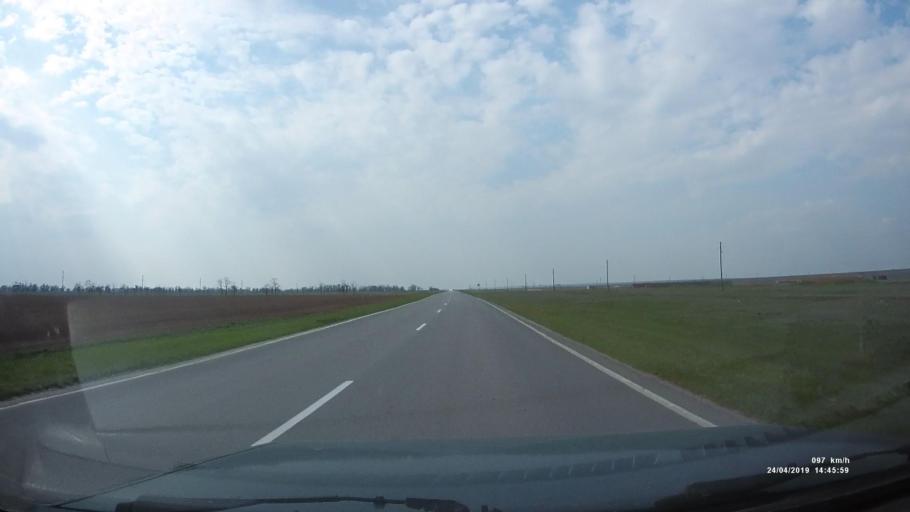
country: RU
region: Rostov
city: Remontnoye
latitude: 46.4776
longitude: 43.7979
